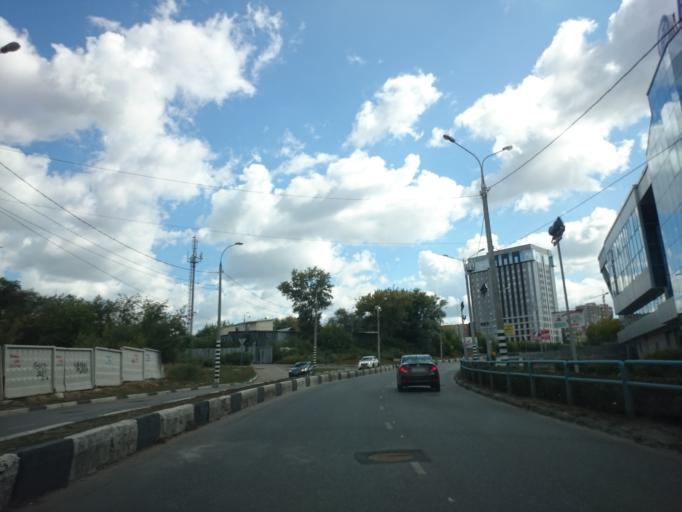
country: RU
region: Samara
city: Samara
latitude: 53.2161
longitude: 50.1349
